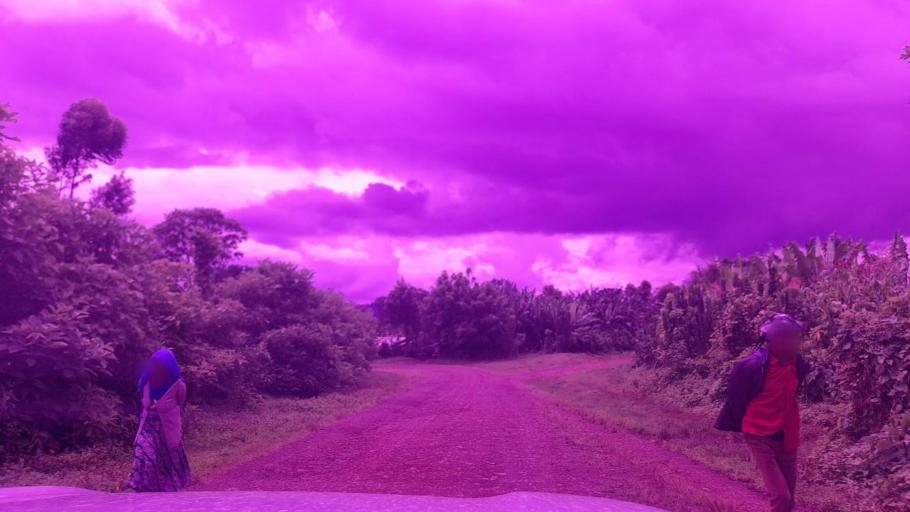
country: ET
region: Southern Nations, Nationalities, and People's Region
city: Tippi
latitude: 7.6329
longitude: 35.5779
